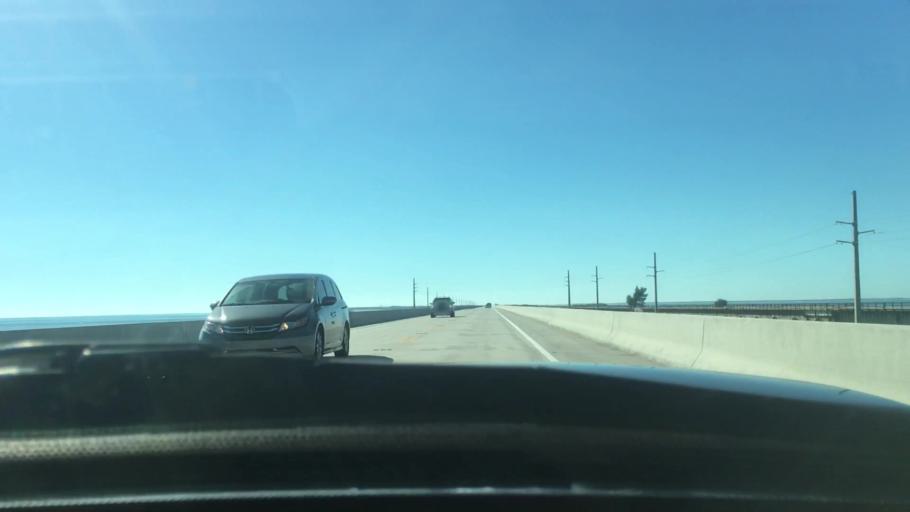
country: US
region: Florida
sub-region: Monroe County
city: Marathon
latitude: 24.6901
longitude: -81.2008
